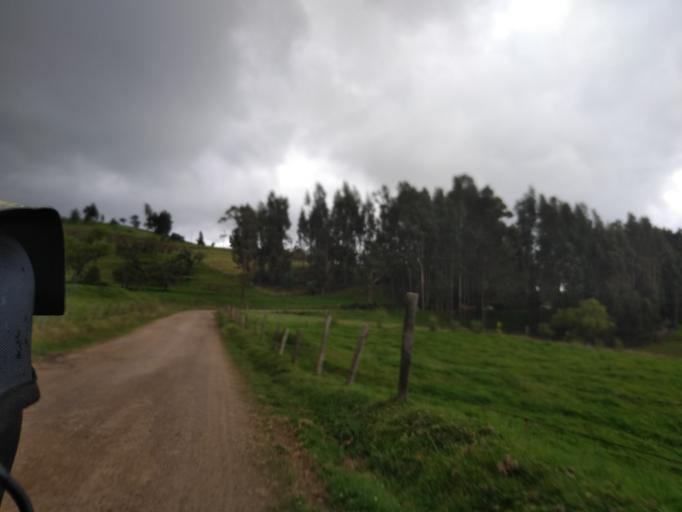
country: CO
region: Boyaca
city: Sotaquira
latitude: 5.7663
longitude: -73.2718
